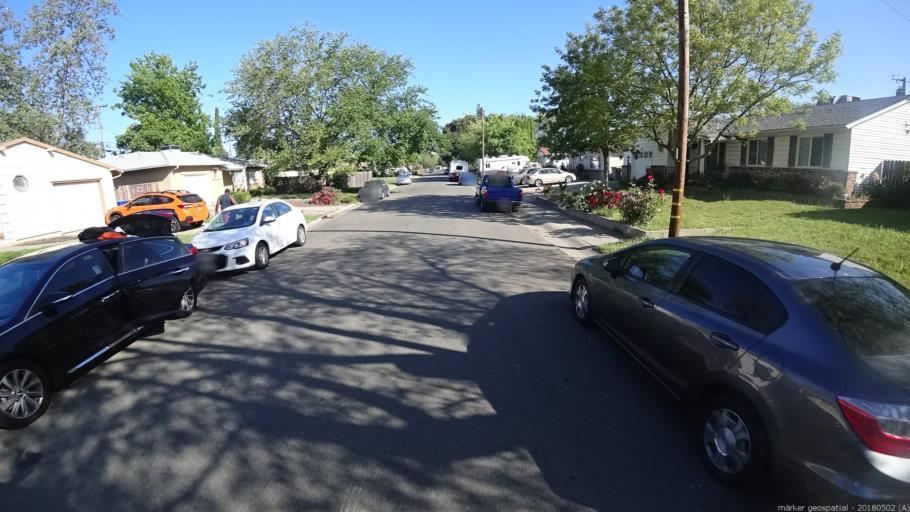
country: US
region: California
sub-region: Sacramento County
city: Arden-Arcade
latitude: 38.6035
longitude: -121.4233
